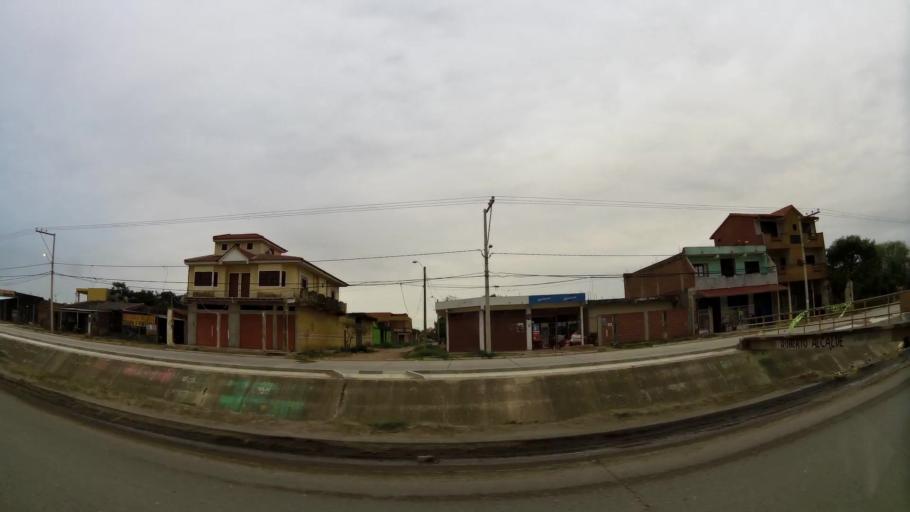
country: BO
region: Santa Cruz
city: Santa Cruz de la Sierra
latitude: -17.8608
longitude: -63.1735
